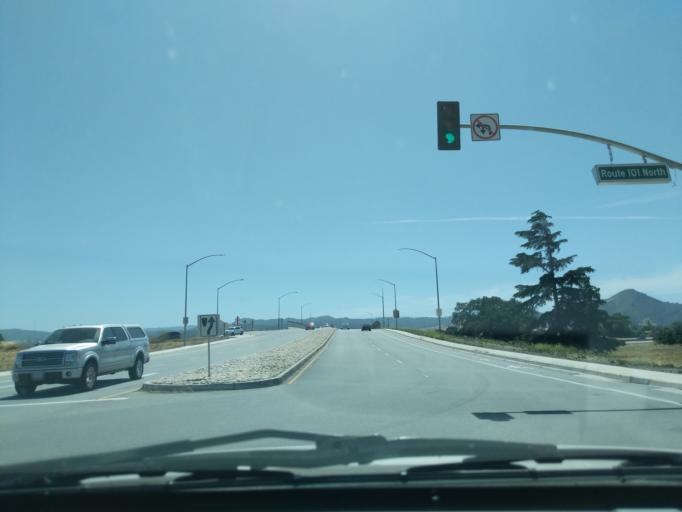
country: US
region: California
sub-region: Santa Clara County
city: Morgan Hill
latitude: 37.1202
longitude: -121.6242
